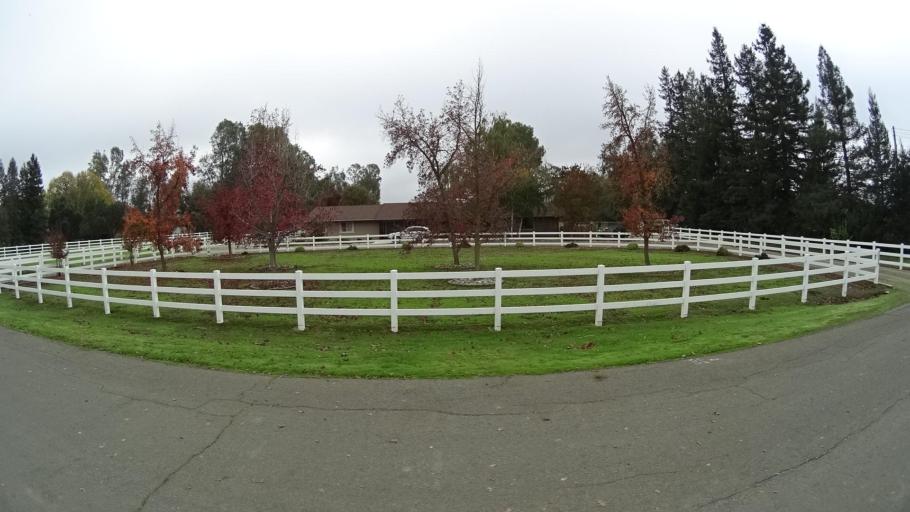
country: US
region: California
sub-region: Sacramento County
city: Elk Grove
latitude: 38.4139
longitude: -121.3284
